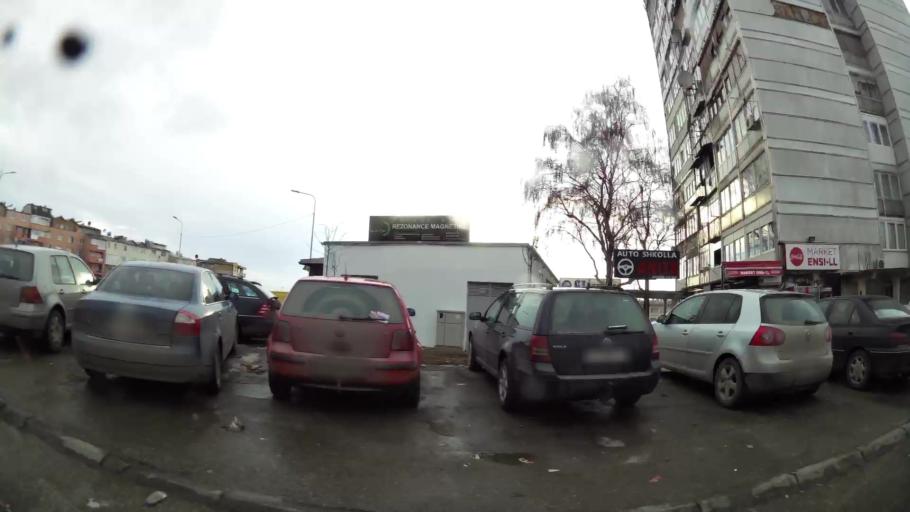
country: XK
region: Pristina
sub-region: Komuna e Prishtines
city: Pristina
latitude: 42.6507
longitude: 21.1624
